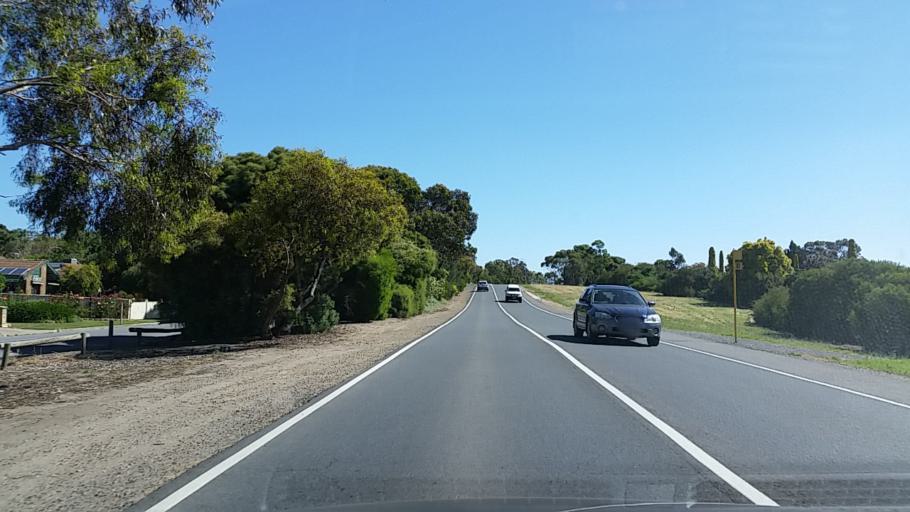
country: AU
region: South Australia
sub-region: Tea Tree Gully
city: Golden Grove
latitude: -34.8003
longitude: 138.7059
